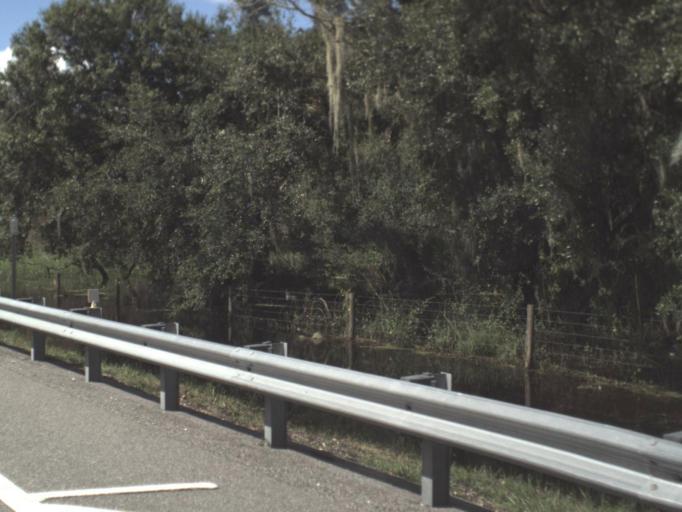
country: US
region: Florida
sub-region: Sarasota County
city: Lake Sarasota
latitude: 27.3797
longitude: -82.2345
